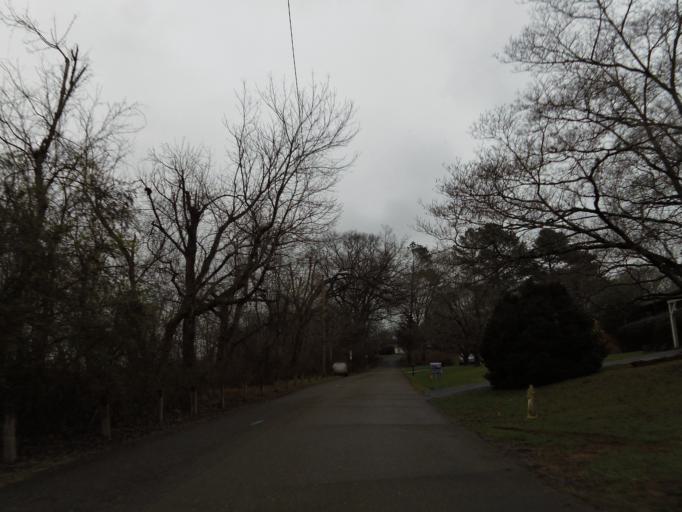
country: US
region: Tennessee
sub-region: Knox County
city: Knoxville
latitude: 35.9615
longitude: -83.8826
